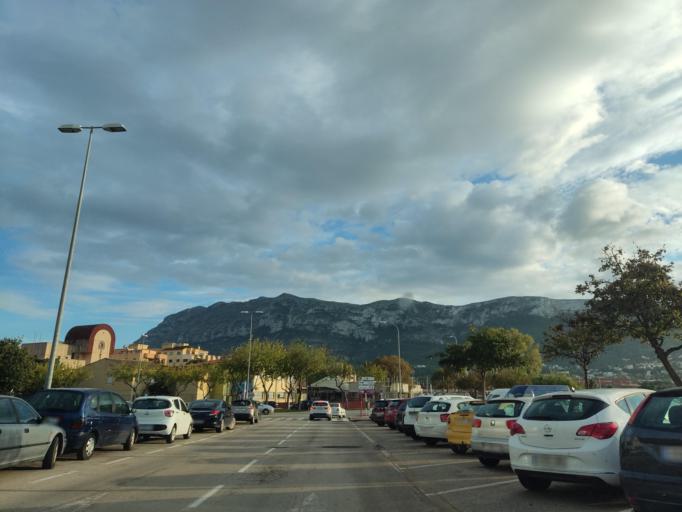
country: ES
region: Valencia
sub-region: Provincia de Alicante
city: Denia
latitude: 38.8361
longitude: 0.1011
